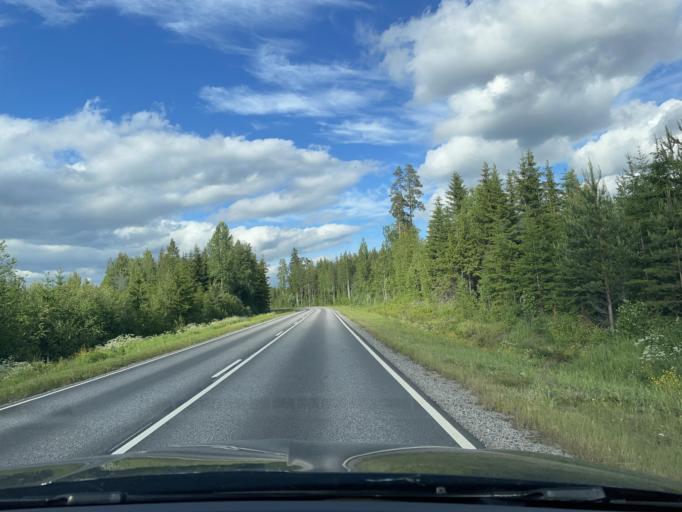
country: FI
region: Central Finland
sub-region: Jyvaeskylae
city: Petaejaevesi
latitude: 62.0933
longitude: 25.1573
